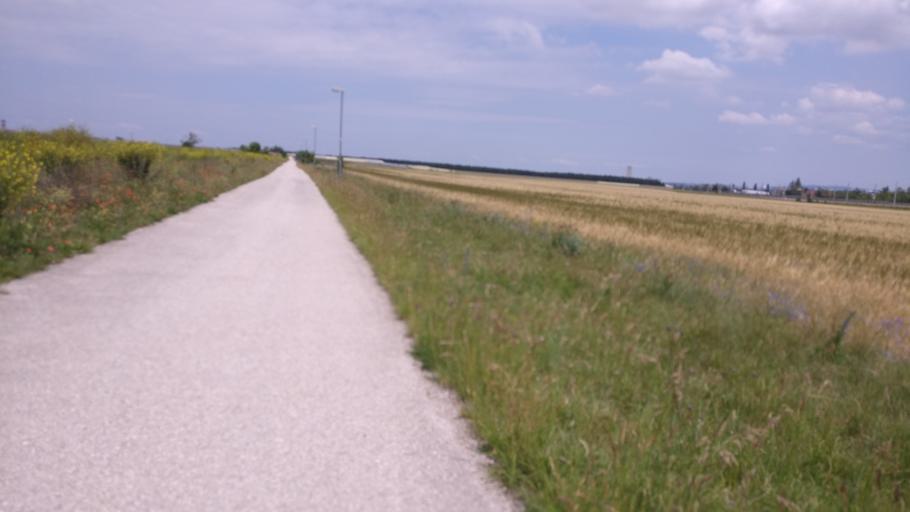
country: AT
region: Lower Austria
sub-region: Politischer Bezirk Wiener Neustadt
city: Lichtenworth
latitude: 47.8383
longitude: 16.2697
